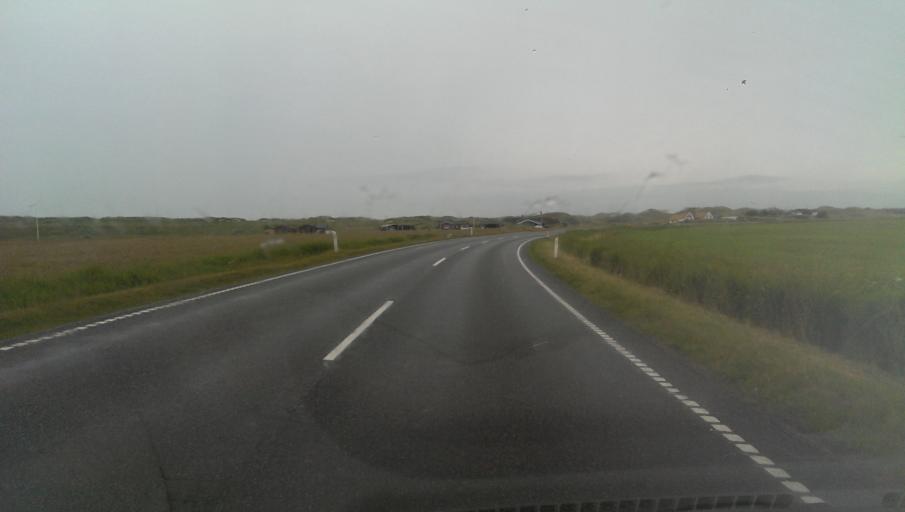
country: DK
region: Central Jutland
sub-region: Ringkobing-Skjern Kommune
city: Ringkobing
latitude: 56.1627
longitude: 8.1225
